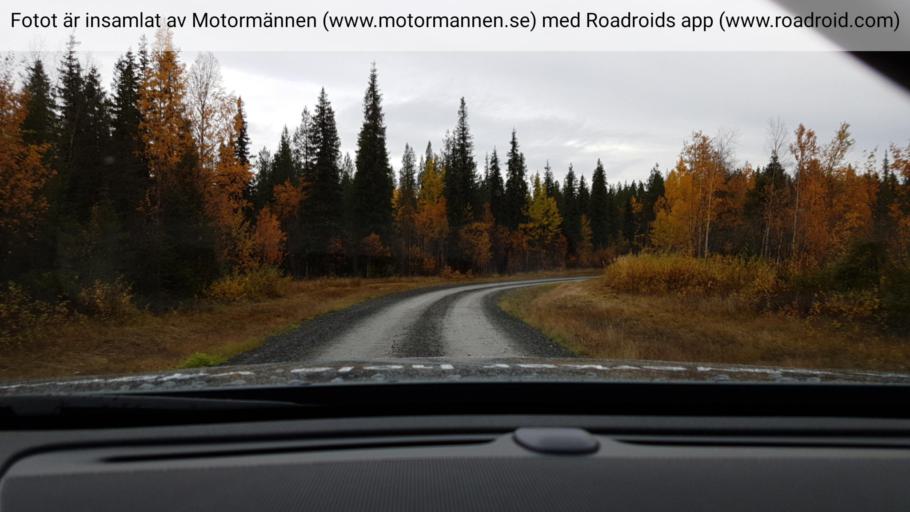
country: SE
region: Norrbotten
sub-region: Pajala Kommun
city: Pajala
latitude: 67.1020
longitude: 22.7069
